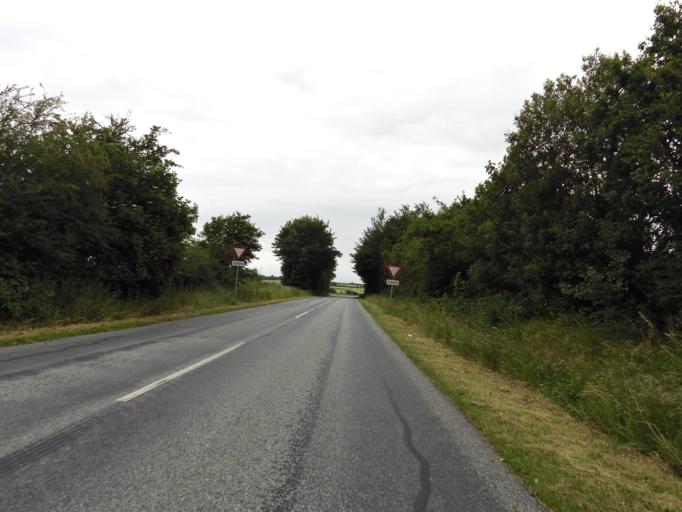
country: DK
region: South Denmark
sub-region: Tonder Kommune
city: Logumkloster
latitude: 55.1407
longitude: 8.9691
